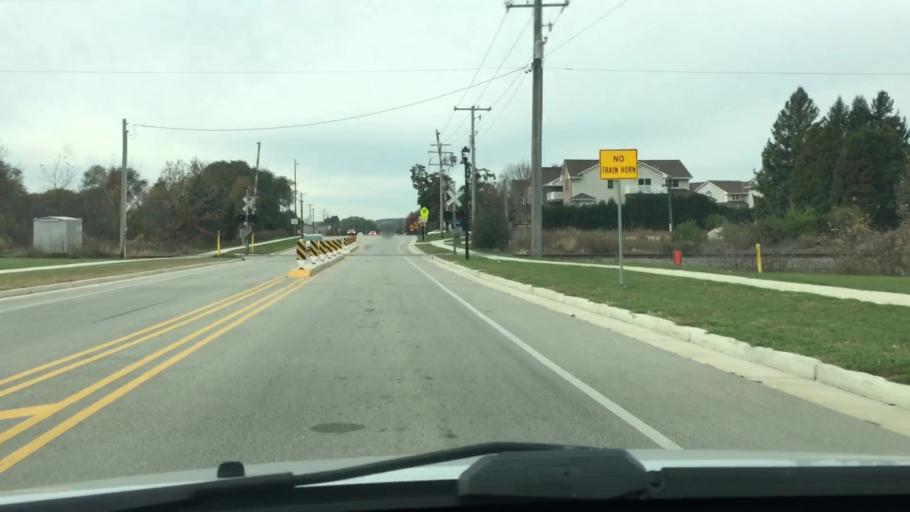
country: US
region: Wisconsin
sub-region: Waukesha County
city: Mukwonago
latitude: 42.8737
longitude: -88.3267
